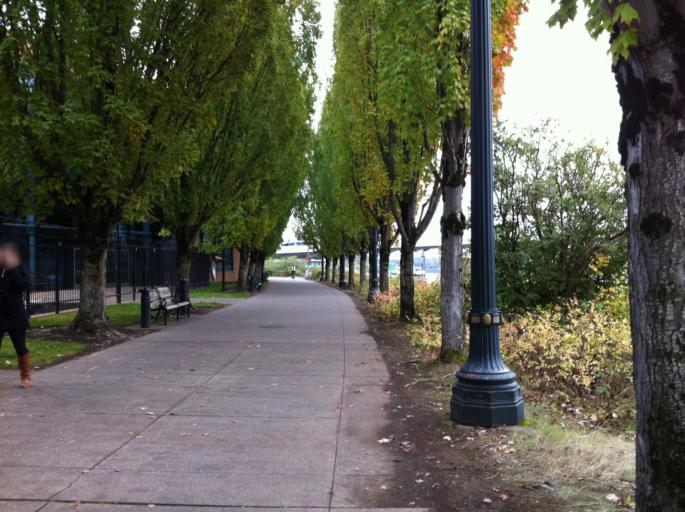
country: US
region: Oregon
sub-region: Multnomah County
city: Portland
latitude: 45.5080
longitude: -122.6663
